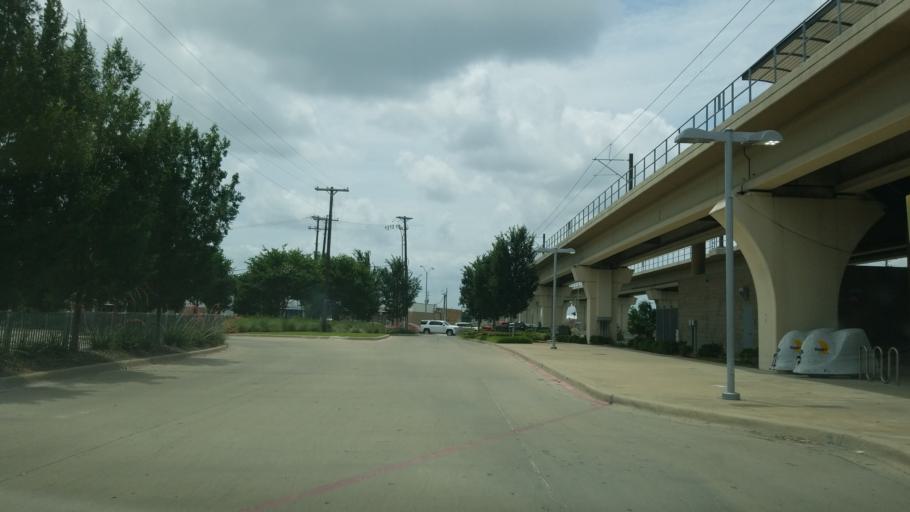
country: US
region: Texas
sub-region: Dallas County
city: Farmers Branch
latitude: 32.8820
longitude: -96.8836
